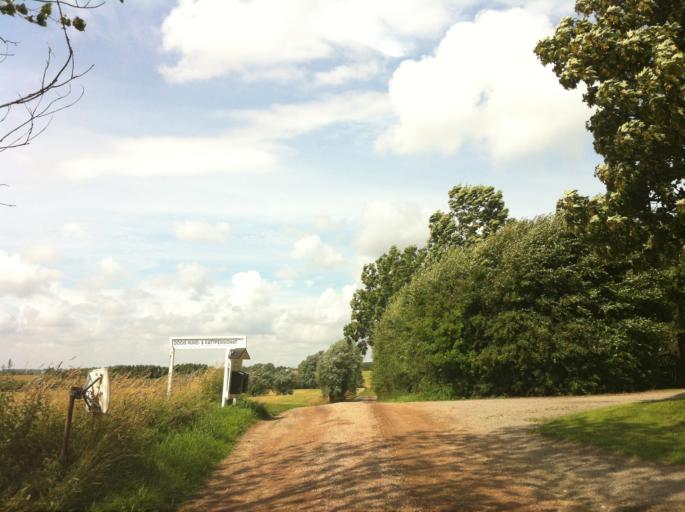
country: SE
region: Skane
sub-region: Skurups Kommun
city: Skurup
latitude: 55.4446
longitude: 13.4389
